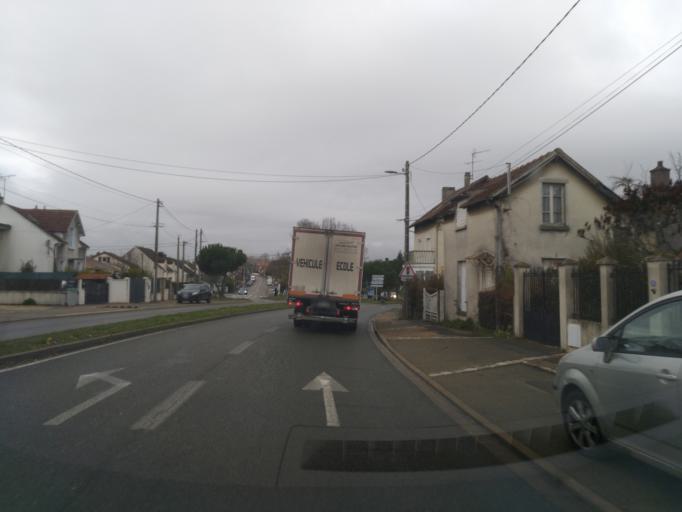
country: FR
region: Ile-de-France
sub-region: Departement des Yvelines
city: Villepreux
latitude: 48.8197
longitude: 2.0005
